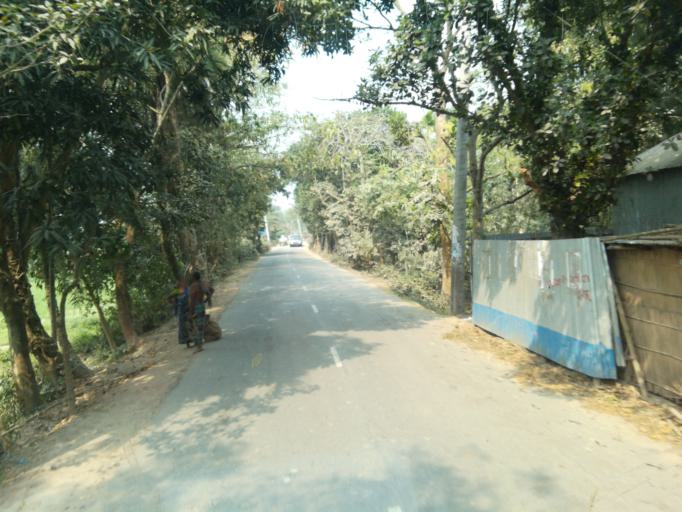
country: BD
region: Dhaka
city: Nagarpur
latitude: 23.9853
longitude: 89.8442
